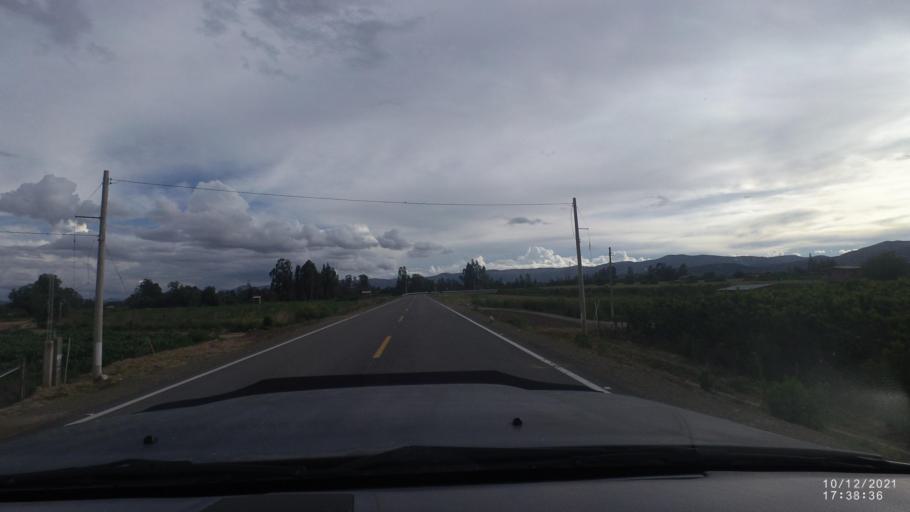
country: BO
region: Cochabamba
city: Tarata
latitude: -17.5717
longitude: -66.0097
